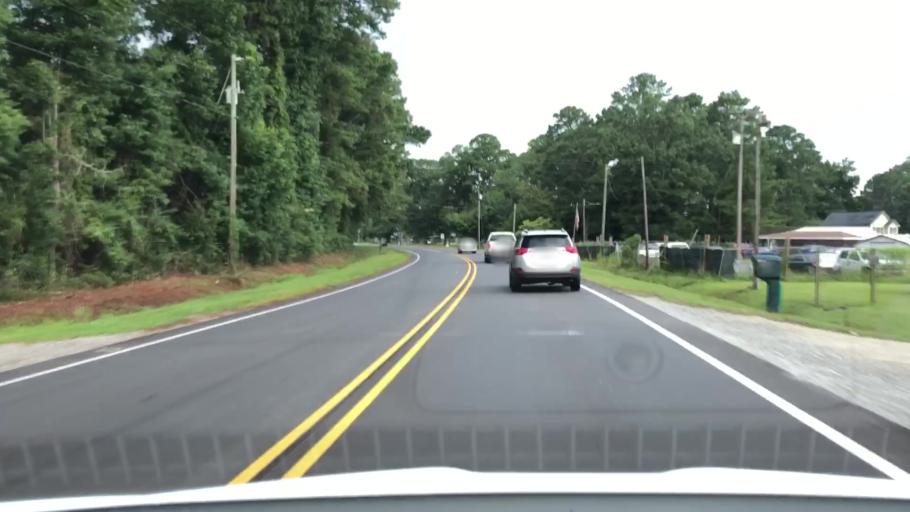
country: US
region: North Carolina
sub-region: Jones County
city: Maysville
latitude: 34.9010
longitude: -77.2251
